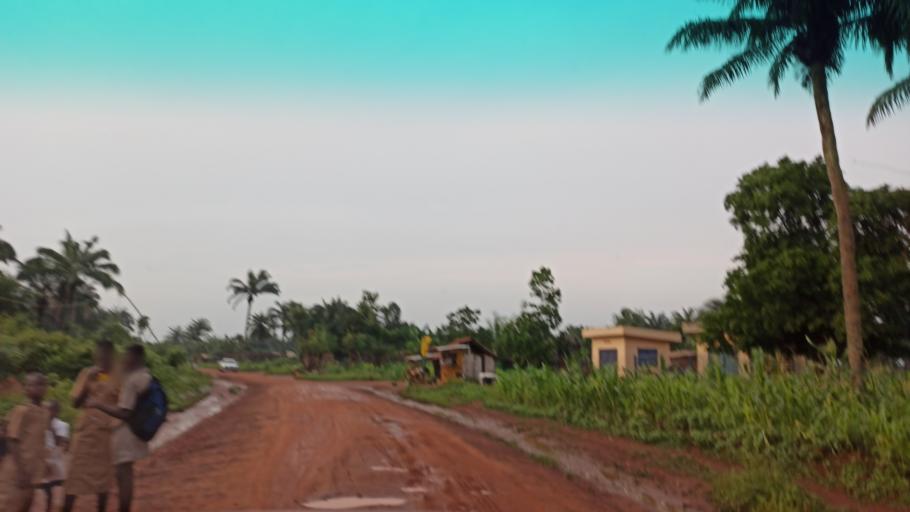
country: BJ
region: Queme
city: Porto-Novo
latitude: 6.5441
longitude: 2.6190
